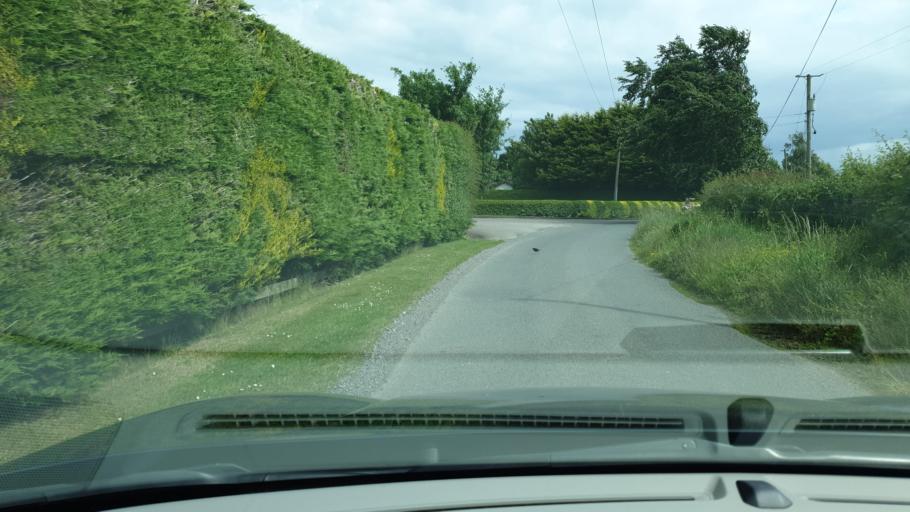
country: IE
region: Leinster
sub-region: An Mhi
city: Dunboyne
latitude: 53.4509
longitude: -6.4446
